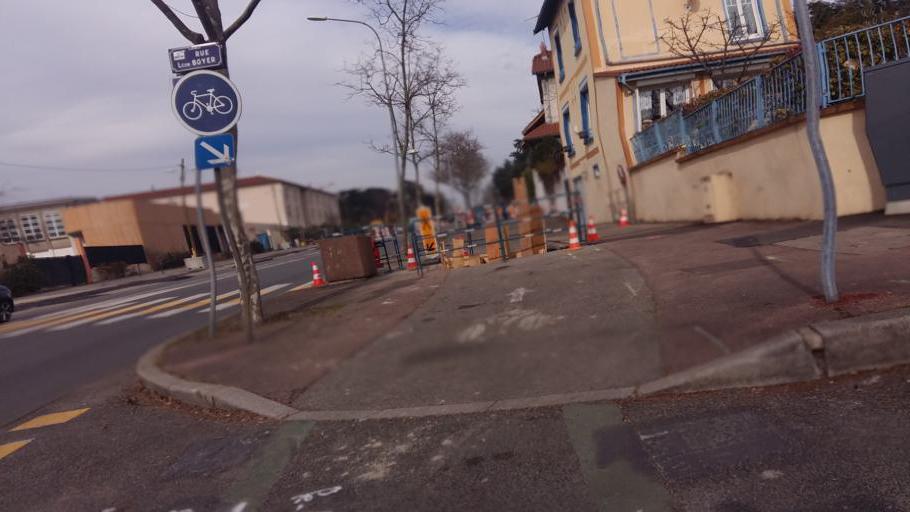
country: FR
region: Rhone-Alpes
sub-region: Departement du Rhone
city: Bron
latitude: 45.7329
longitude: 4.8887
